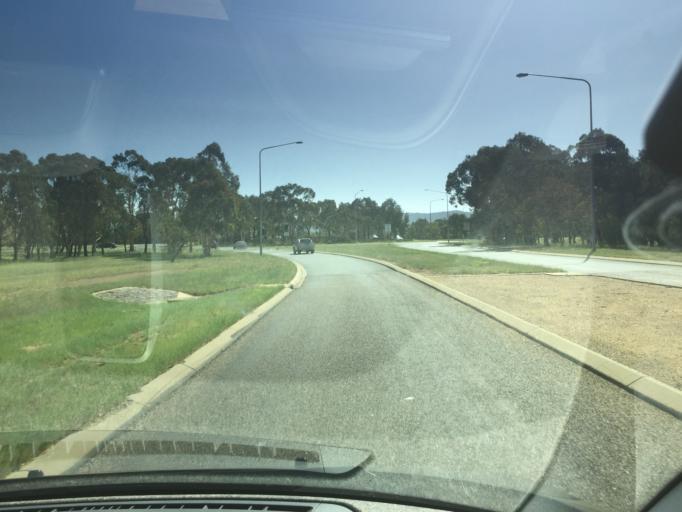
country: AU
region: Australian Capital Territory
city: Macarthur
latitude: -35.4231
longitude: 149.0801
